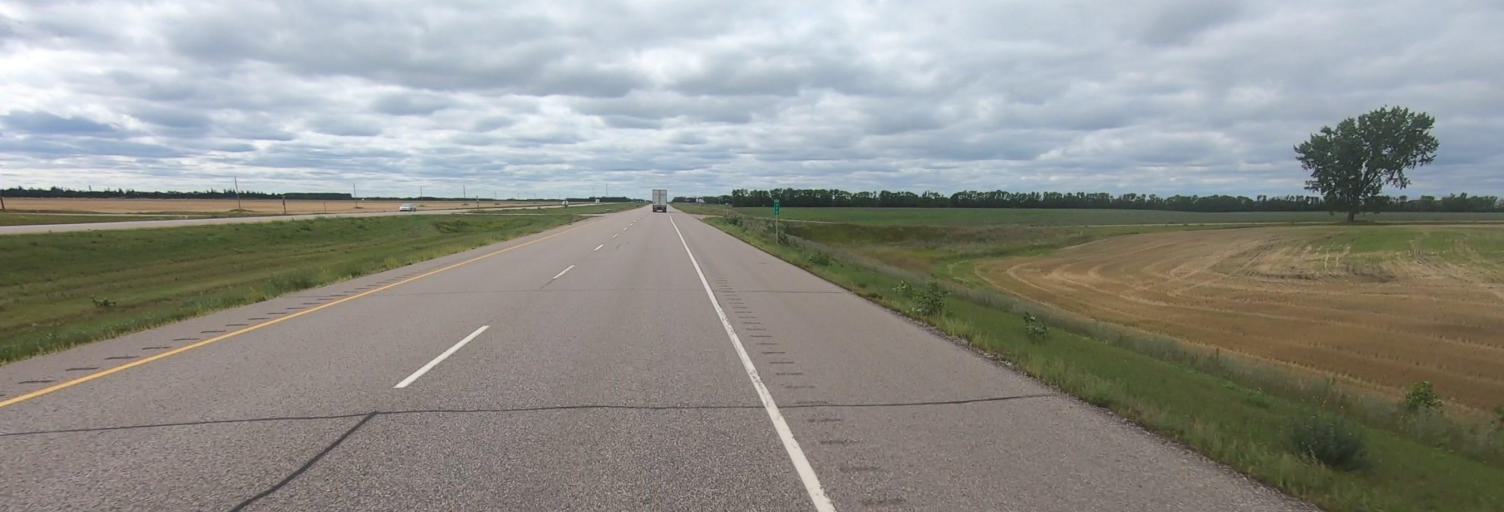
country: CA
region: Manitoba
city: Carberry
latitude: 49.9014
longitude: -99.2921
